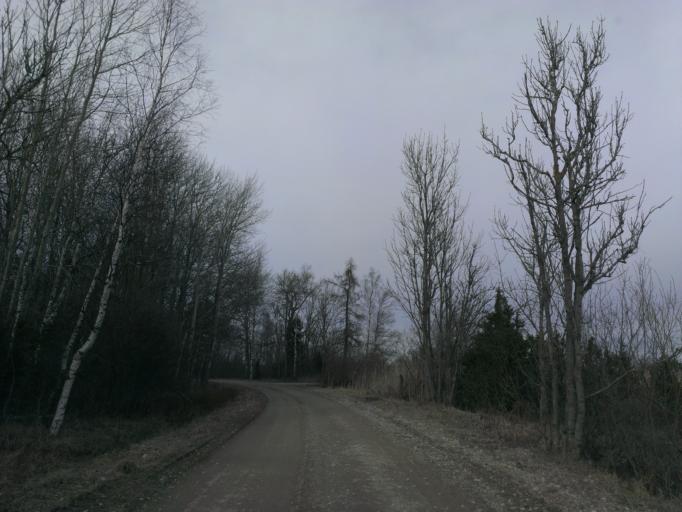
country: EE
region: Laeaene
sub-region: Lihula vald
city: Lihula
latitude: 58.5711
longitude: 23.5489
